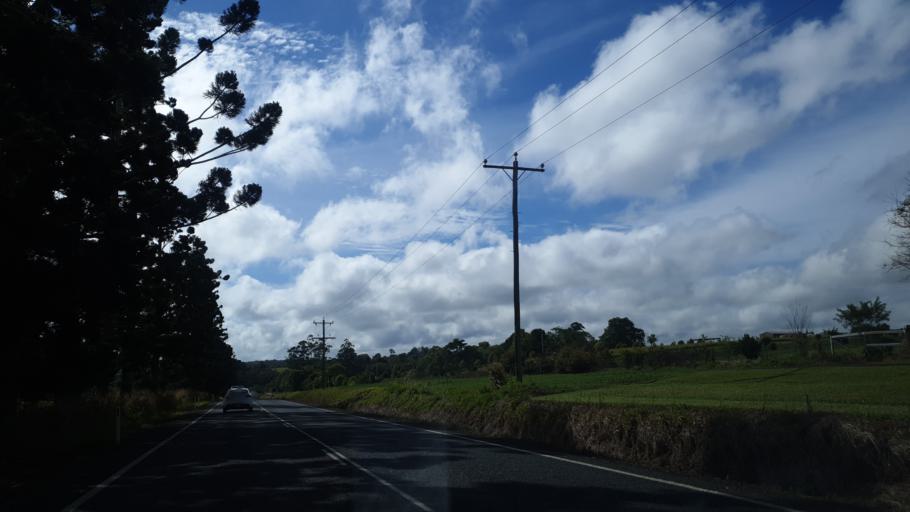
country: AU
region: Queensland
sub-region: Tablelands
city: Atherton
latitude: -17.3419
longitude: 145.5702
